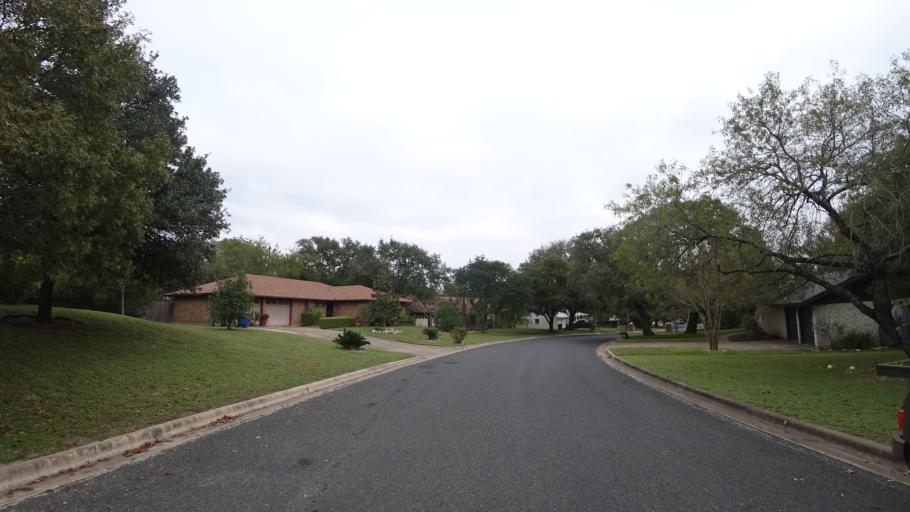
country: US
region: Texas
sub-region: Travis County
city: Barton Creek
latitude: 30.2364
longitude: -97.8816
